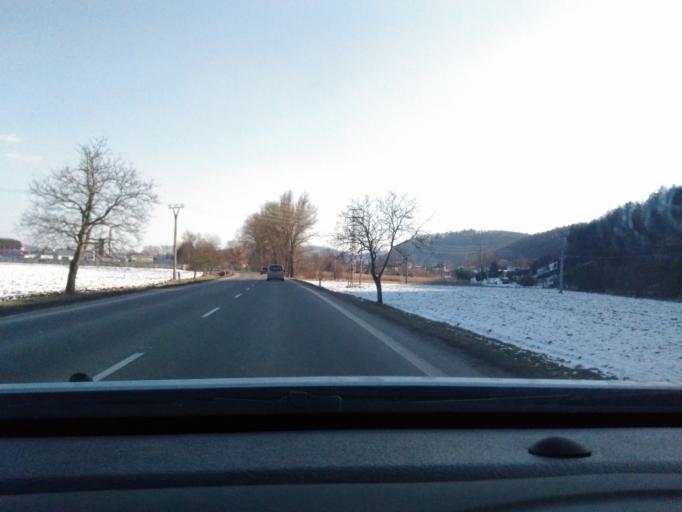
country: CZ
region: South Moravian
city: Tisnov
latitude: 49.3450
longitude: 16.4136
